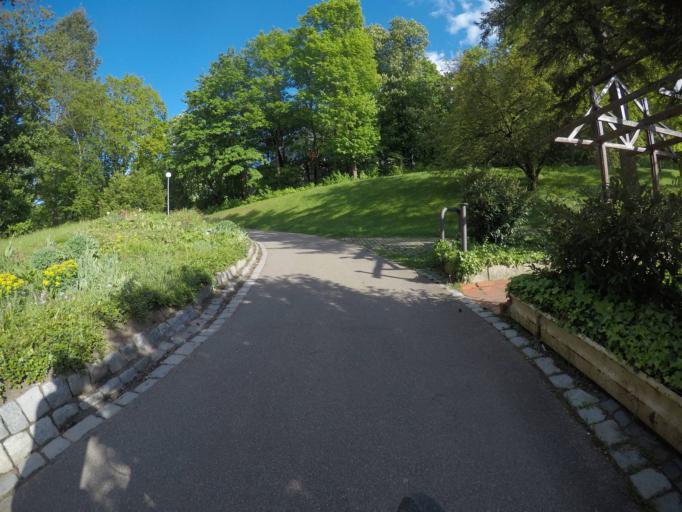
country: DE
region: Baden-Wuerttemberg
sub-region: Regierungsbezirk Stuttgart
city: Stuttgart-Ost
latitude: 48.7943
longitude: 9.2070
